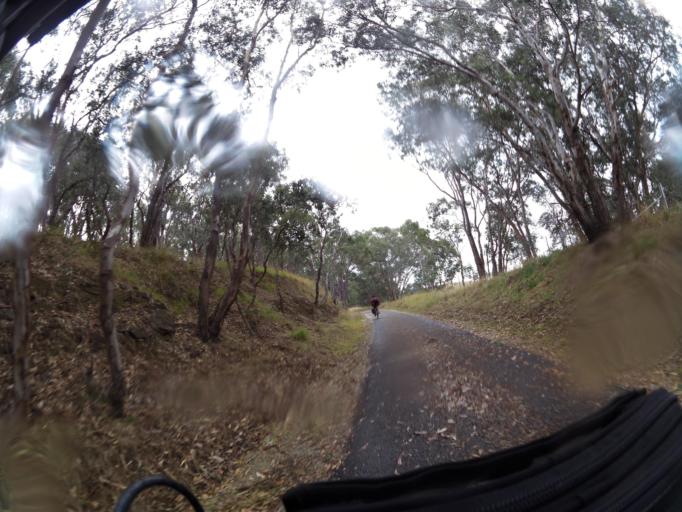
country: AU
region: New South Wales
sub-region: Albury Municipality
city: East Albury
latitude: -36.2145
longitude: 147.2406
